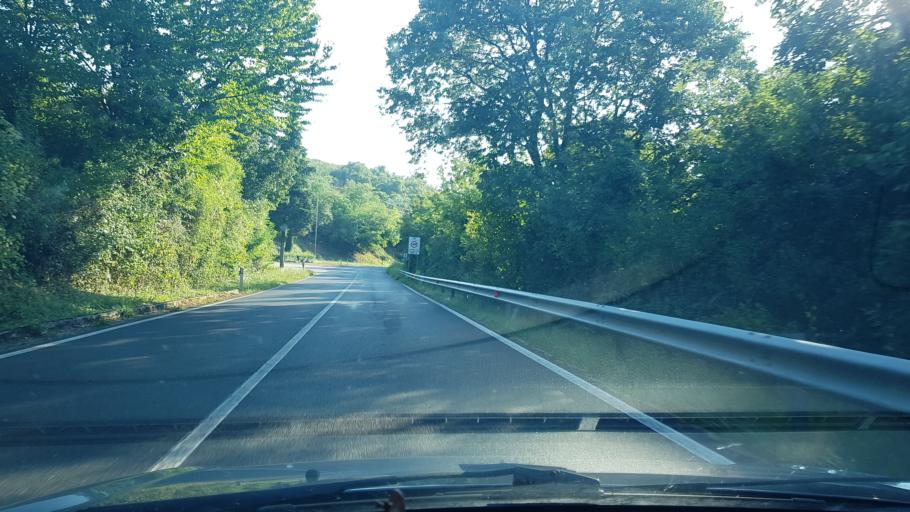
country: IT
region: Friuli Venezia Giulia
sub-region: Provincia di Gorizia
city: Savogna d'Isonzo
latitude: 45.8978
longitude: 13.5501
